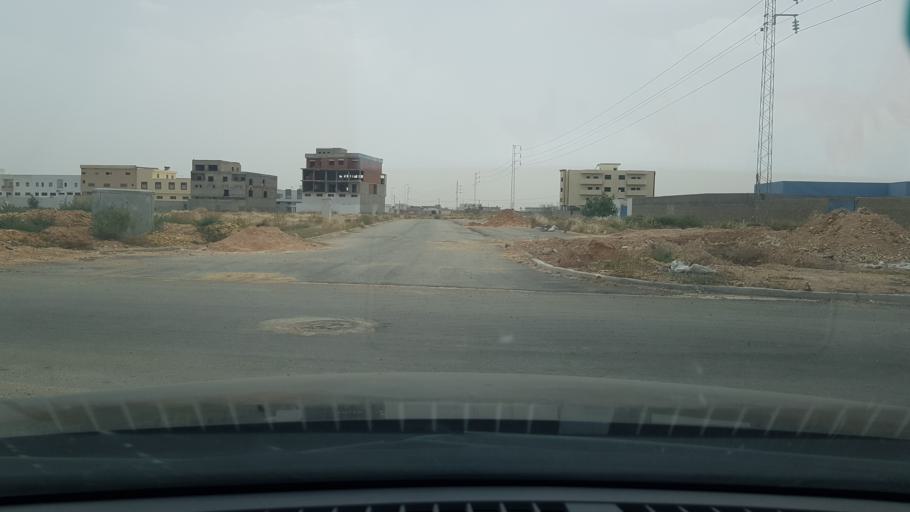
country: TN
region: Safaqis
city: Al Qarmadah
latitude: 34.8293
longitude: 10.7411
